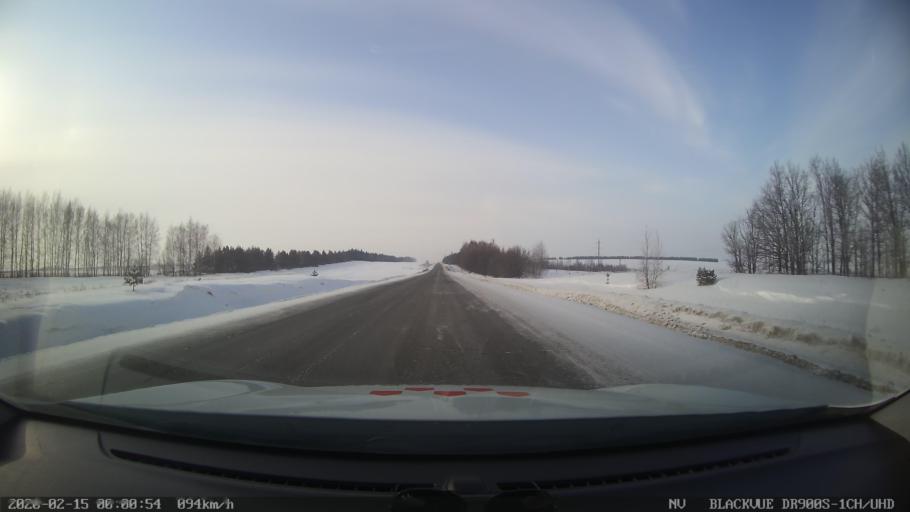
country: RU
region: Tatarstan
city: Kuybyshevskiy Zaton
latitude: 55.3446
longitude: 49.0278
